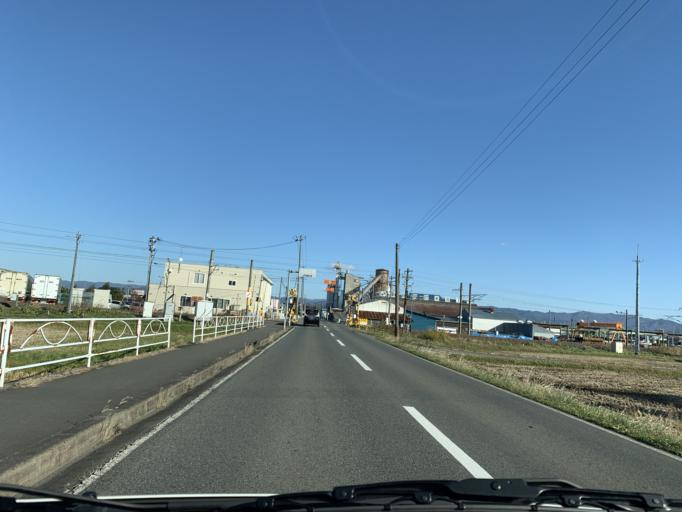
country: JP
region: Iwate
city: Mizusawa
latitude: 39.1650
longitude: 141.1380
